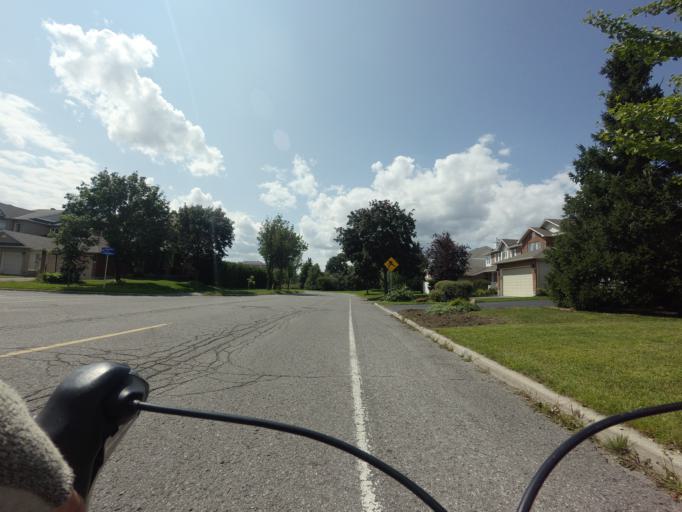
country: CA
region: Ontario
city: Bells Corners
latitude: 45.2763
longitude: -75.8583
